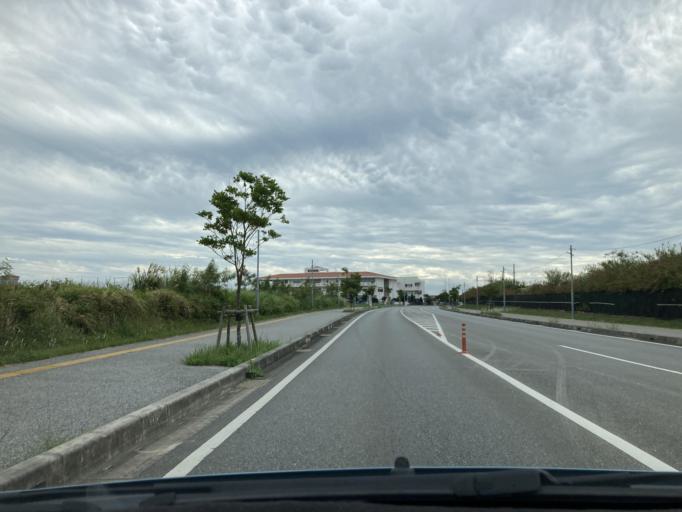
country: JP
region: Okinawa
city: Ishikawa
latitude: 26.3986
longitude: 127.7403
